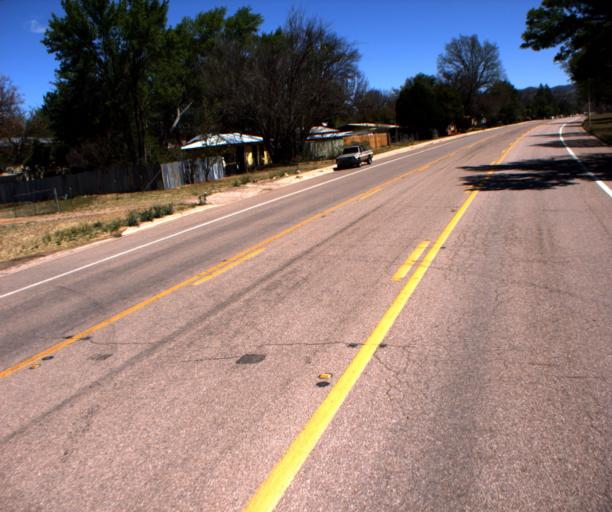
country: US
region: Arizona
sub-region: Santa Cruz County
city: Rio Rico
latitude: 31.5378
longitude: -110.7587
